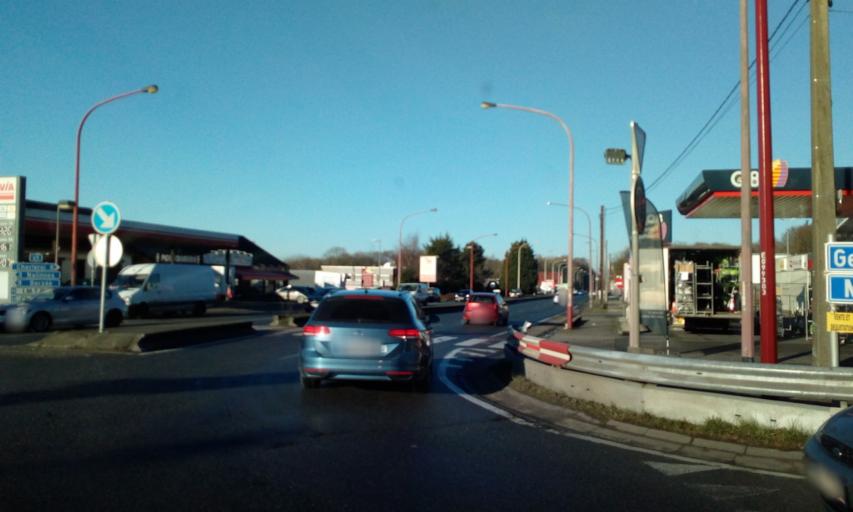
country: BE
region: Wallonia
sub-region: Province du Hainaut
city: Gerpinnes
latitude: 50.3434
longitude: 4.4735
